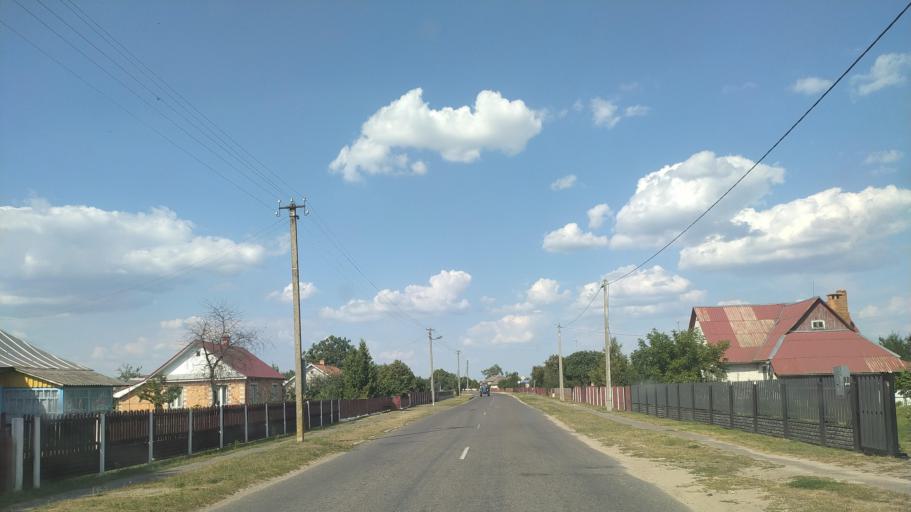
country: BY
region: Brest
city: Drahichyn
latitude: 52.1180
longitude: 25.1166
